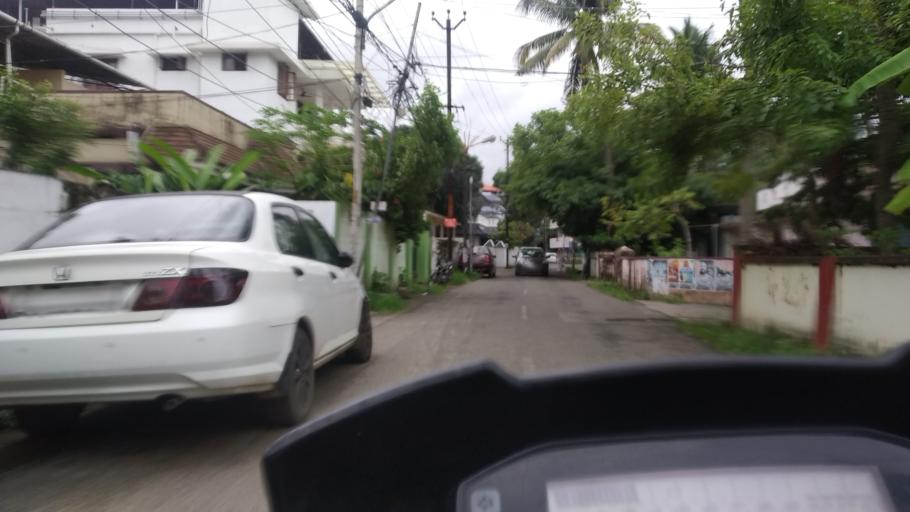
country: IN
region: Kerala
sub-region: Ernakulam
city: Cochin
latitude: 9.9855
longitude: 76.2985
